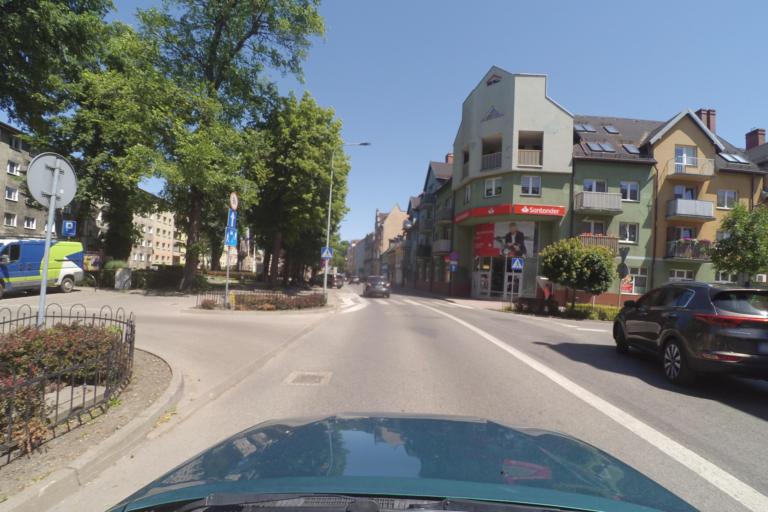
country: PL
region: Lower Silesian Voivodeship
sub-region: Powiat kamiennogorski
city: Kamienna Gora
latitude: 50.7818
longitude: 16.0327
